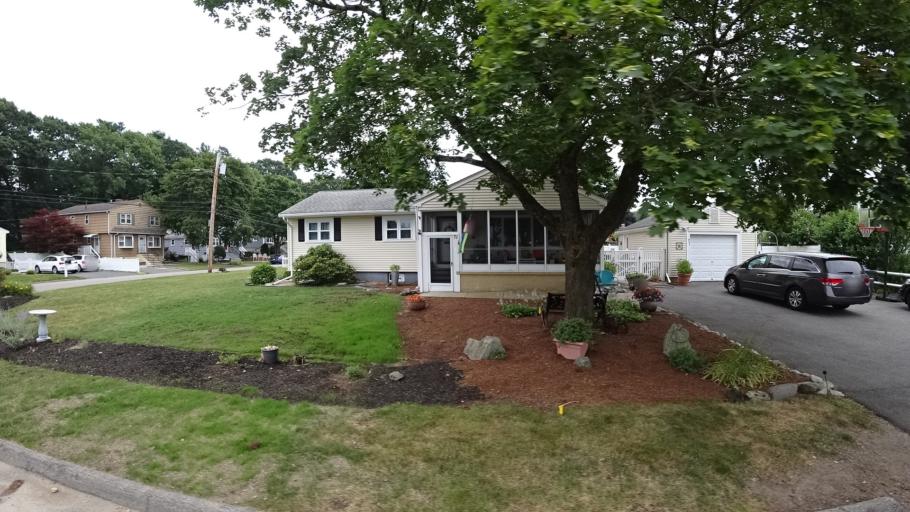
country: US
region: Massachusetts
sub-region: Norfolk County
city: Dedham
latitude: 42.2248
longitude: -71.1635
